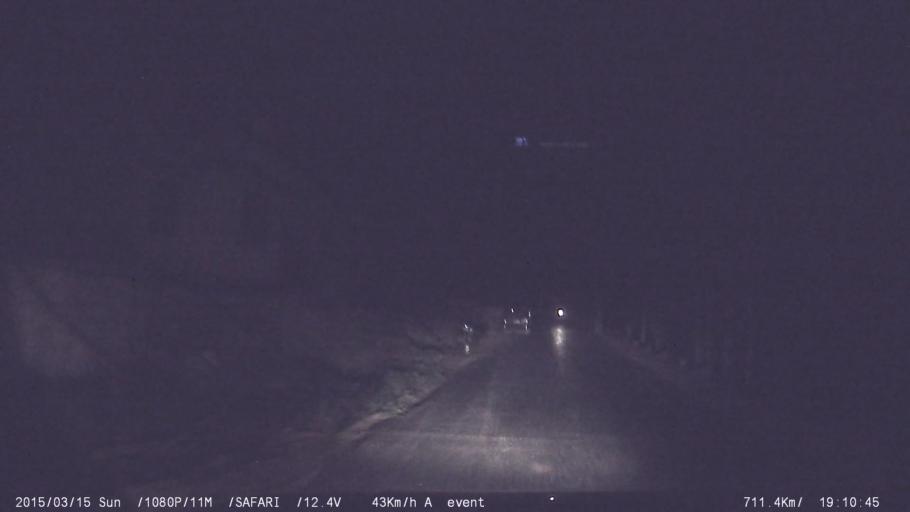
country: IN
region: Kerala
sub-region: Ernakulam
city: Muvattupuzha
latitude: 9.8730
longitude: 76.6156
